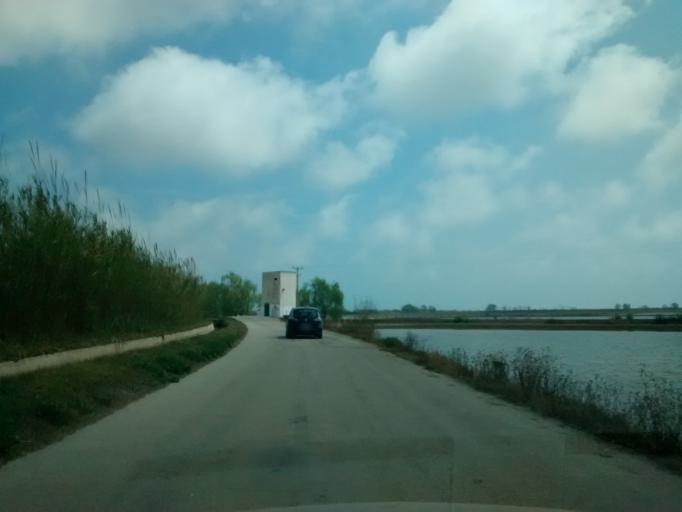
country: ES
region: Catalonia
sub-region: Provincia de Tarragona
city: Deltebre
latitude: 40.6989
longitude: 0.8284
